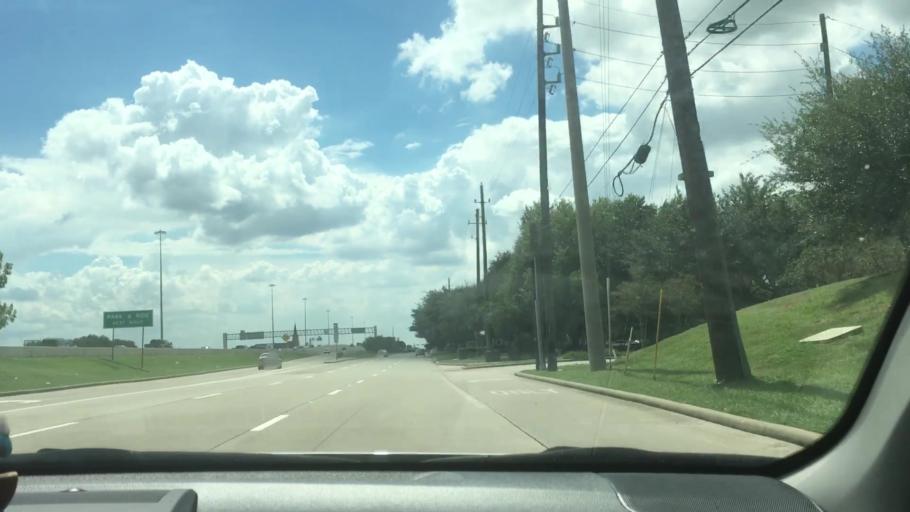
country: US
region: Texas
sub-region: Fort Bend County
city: Sugar Land
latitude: 29.5931
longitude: -95.6296
